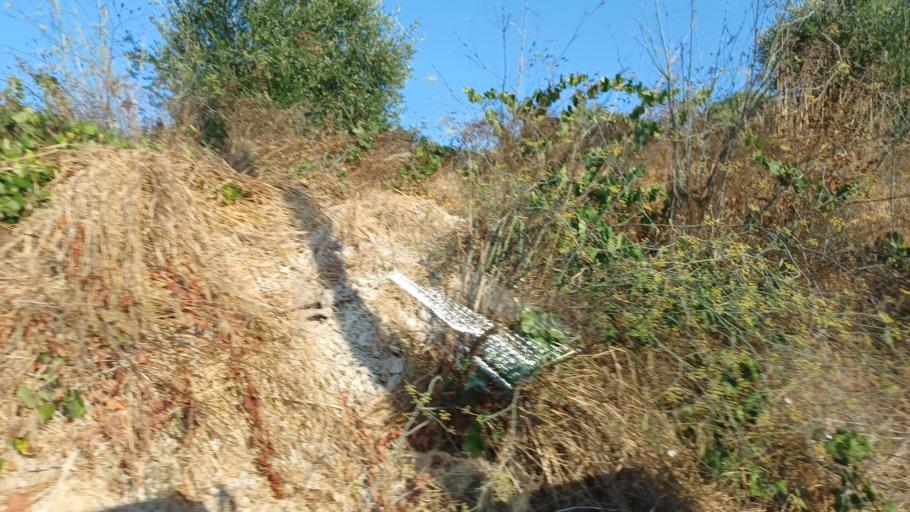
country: CY
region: Pafos
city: Tala
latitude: 34.8906
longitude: 32.4879
